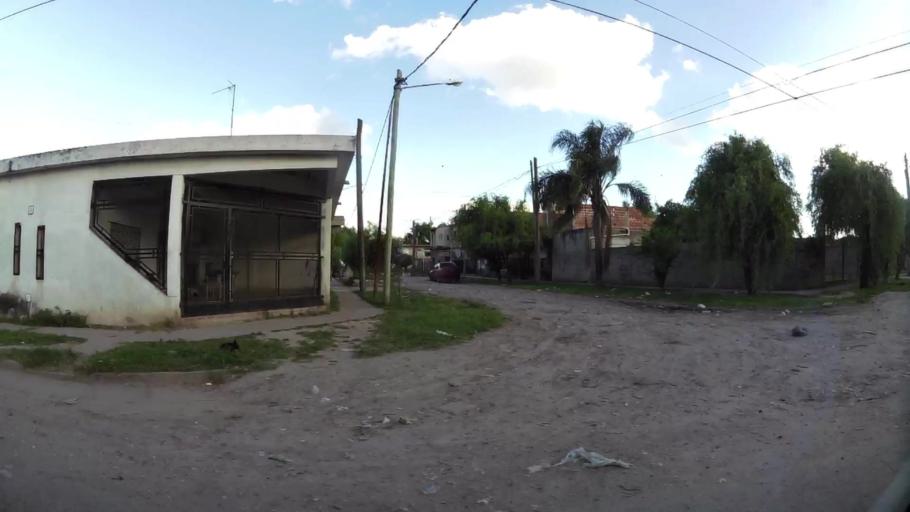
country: AR
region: Buenos Aires
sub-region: Partido de Moron
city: Moron
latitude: -34.7092
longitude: -58.6175
